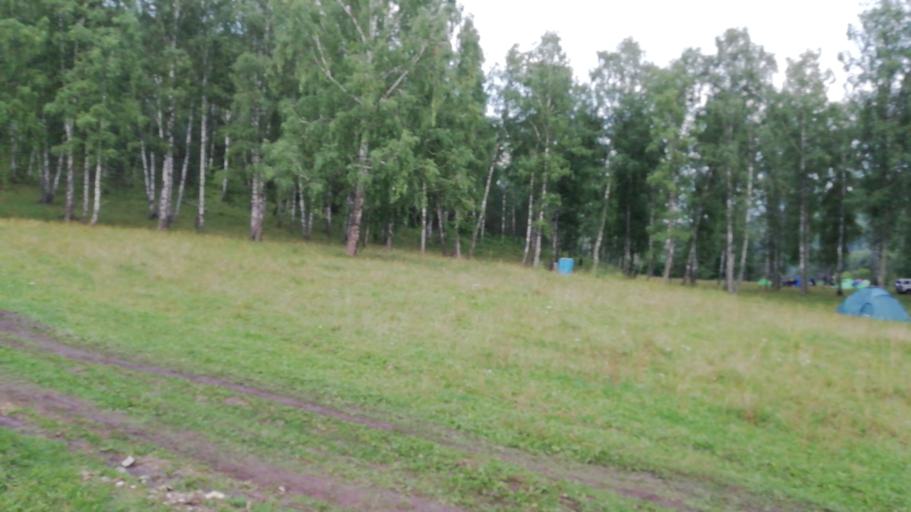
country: RU
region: Chelyabinsk
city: Mezhevoy
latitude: 55.1716
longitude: 58.6475
